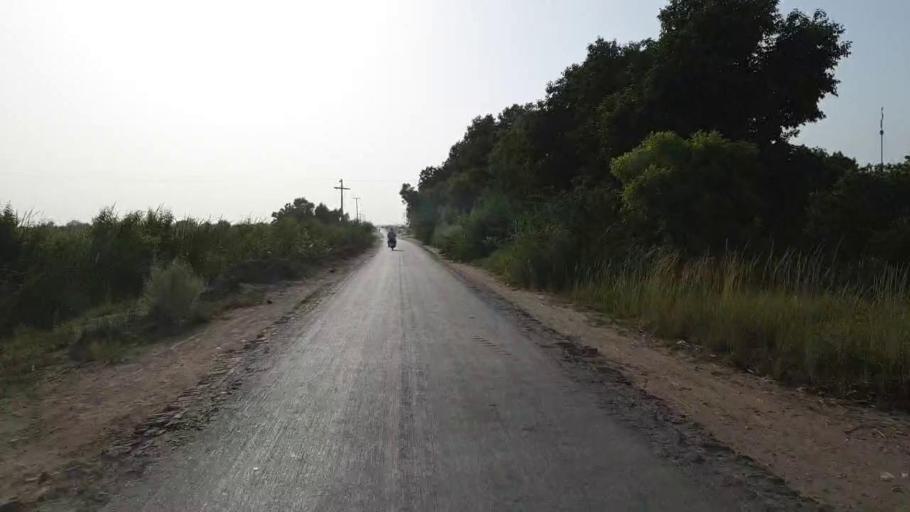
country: PK
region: Sindh
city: Jam Sahib
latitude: 26.4355
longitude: 68.8732
